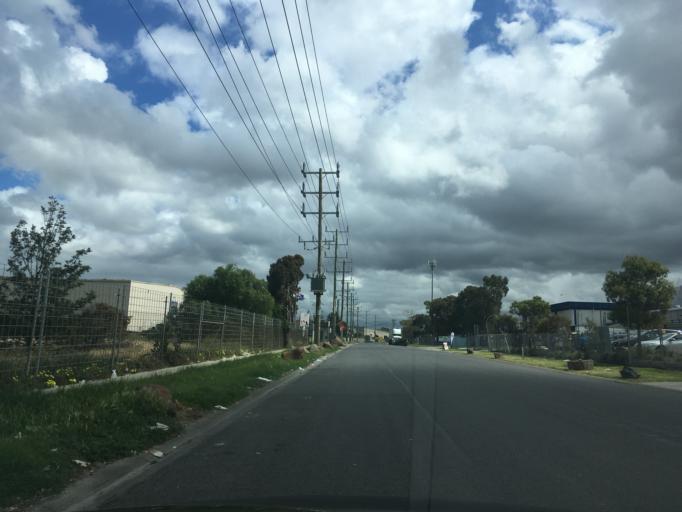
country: AU
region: Victoria
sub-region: Brimbank
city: Derrimut
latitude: -37.8219
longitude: 144.7937
